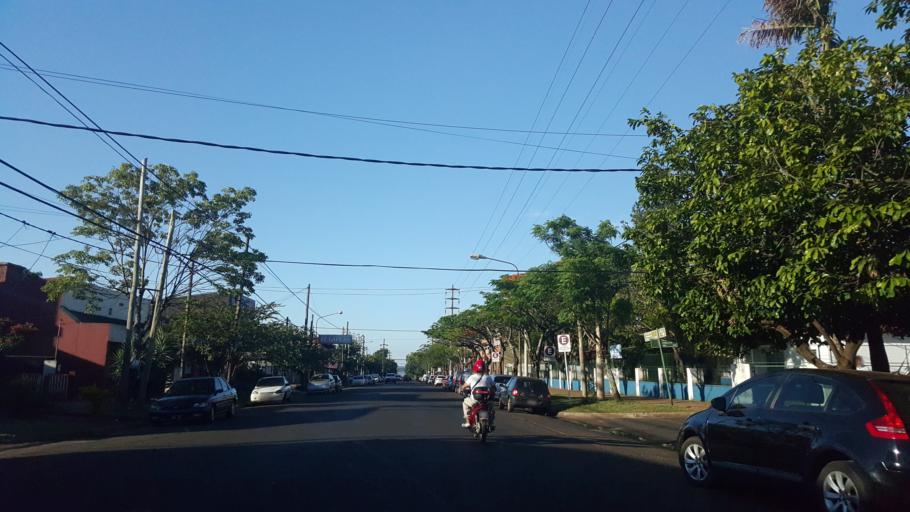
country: AR
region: Misiones
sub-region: Departamento de Capital
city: Posadas
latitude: -27.3690
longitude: -55.9054
